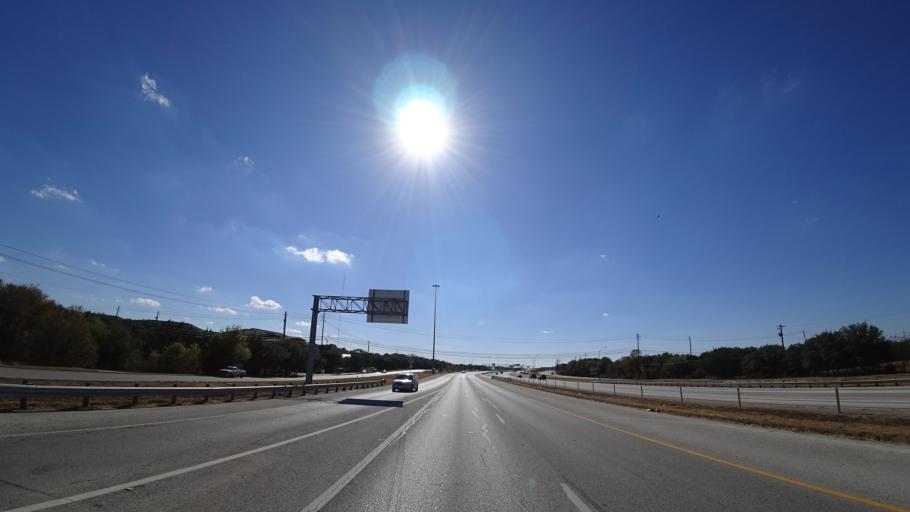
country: US
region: Texas
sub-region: Travis County
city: Rollingwood
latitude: 30.2317
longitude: -97.8267
